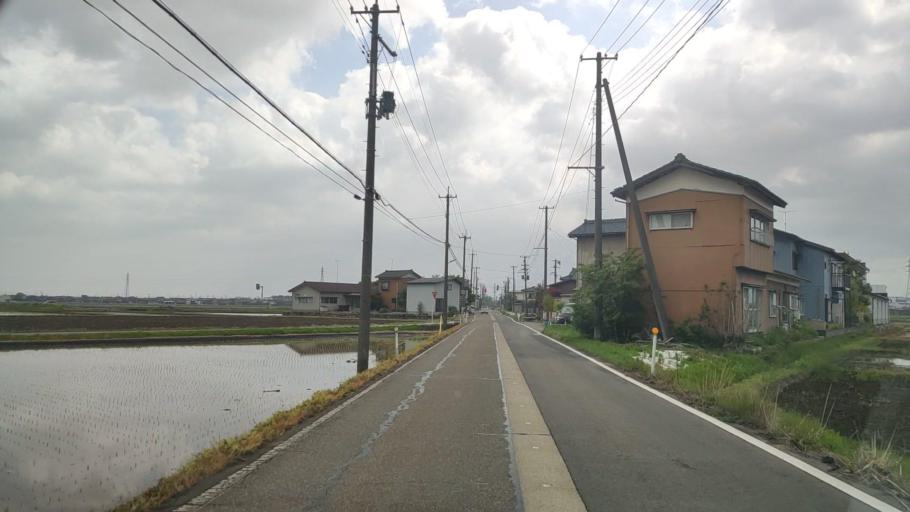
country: JP
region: Niigata
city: Gosen
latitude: 37.7340
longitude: 139.1646
